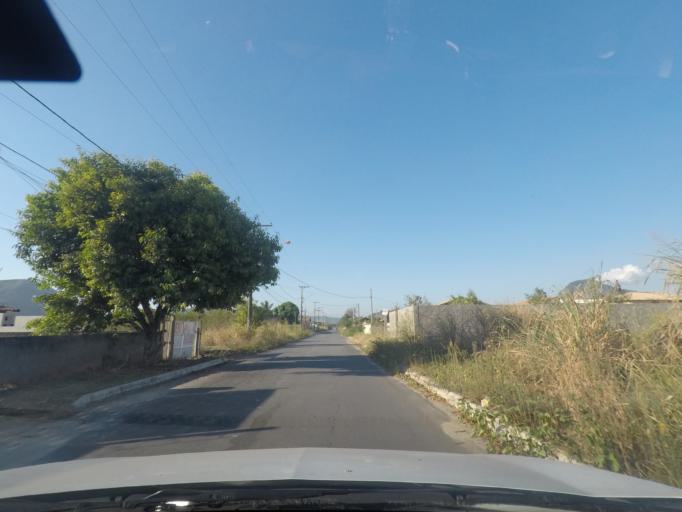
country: BR
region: Rio de Janeiro
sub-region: Marica
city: Marica
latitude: -22.9607
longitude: -42.9388
